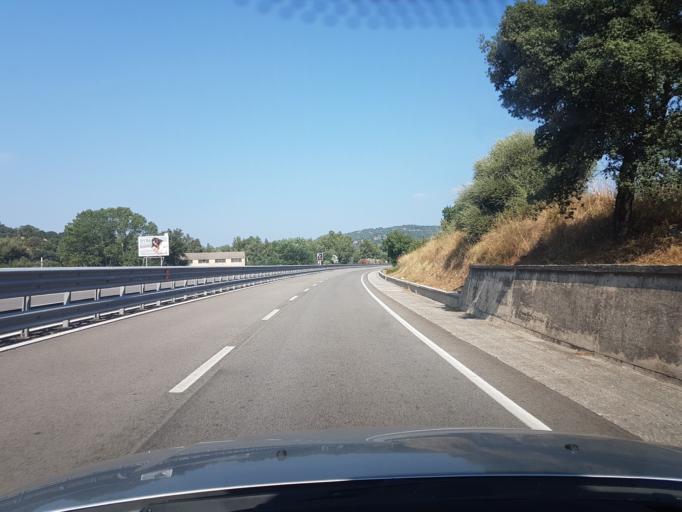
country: IT
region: Sardinia
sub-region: Provincia di Nuoro
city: Oniferi
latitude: 40.3137
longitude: 9.2346
